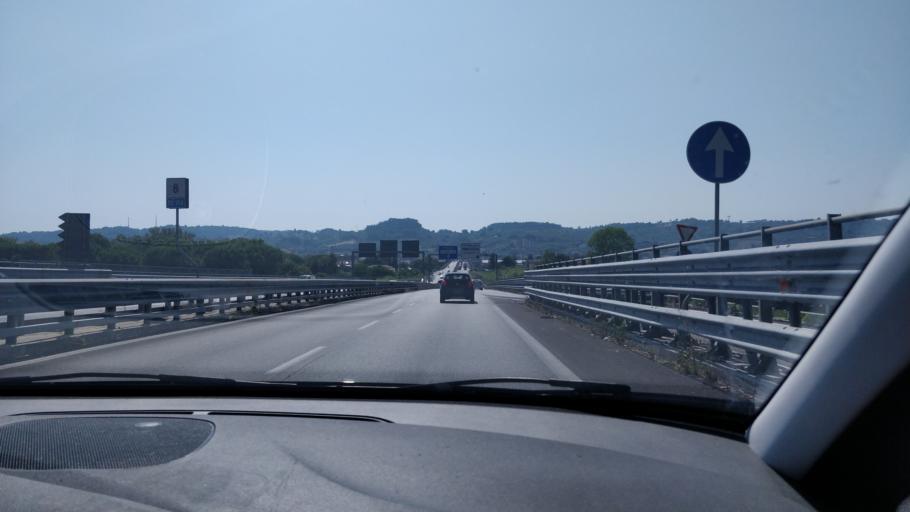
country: IT
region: Abruzzo
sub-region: Provincia di Pescara
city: Villa Raspa
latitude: 42.4451
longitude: 14.1890
